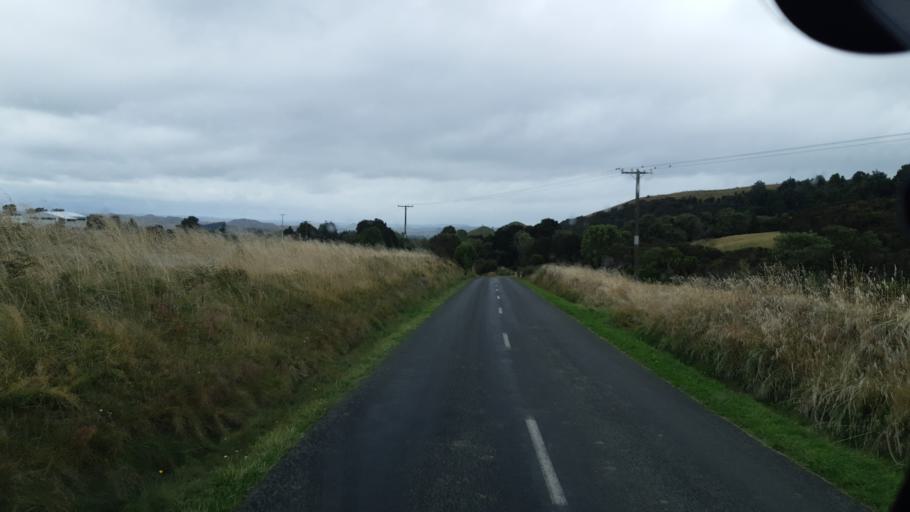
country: NZ
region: Manawatu-Wanganui
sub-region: Ruapehu District
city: Waiouru
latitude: -39.5528
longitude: 175.6434
